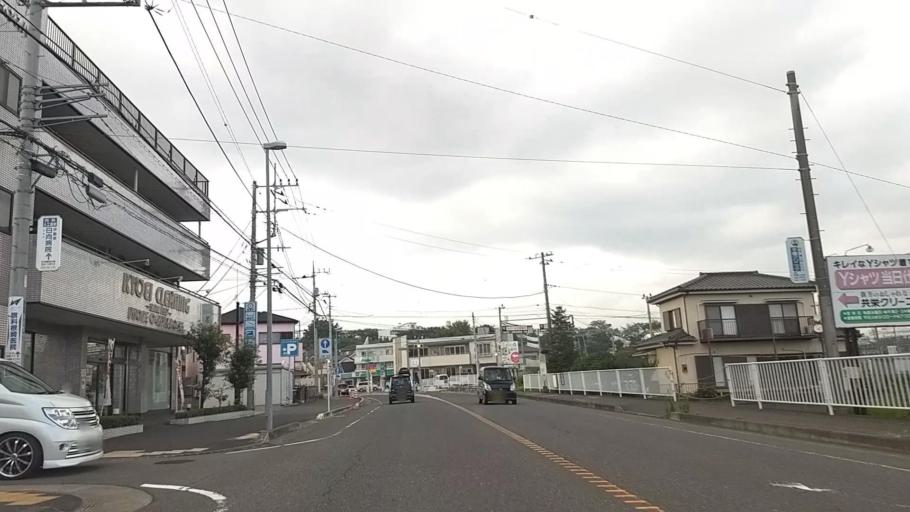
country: JP
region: Kanagawa
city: Isehara
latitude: 35.3863
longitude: 139.3162
